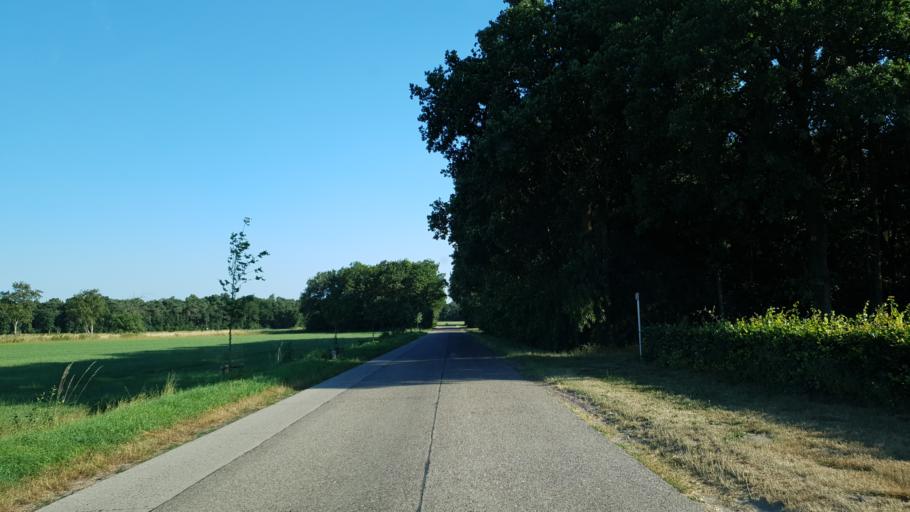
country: BE
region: Flanders
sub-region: Provincie Antwerpen
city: Merksplas
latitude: 51.3915
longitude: 4.8586
